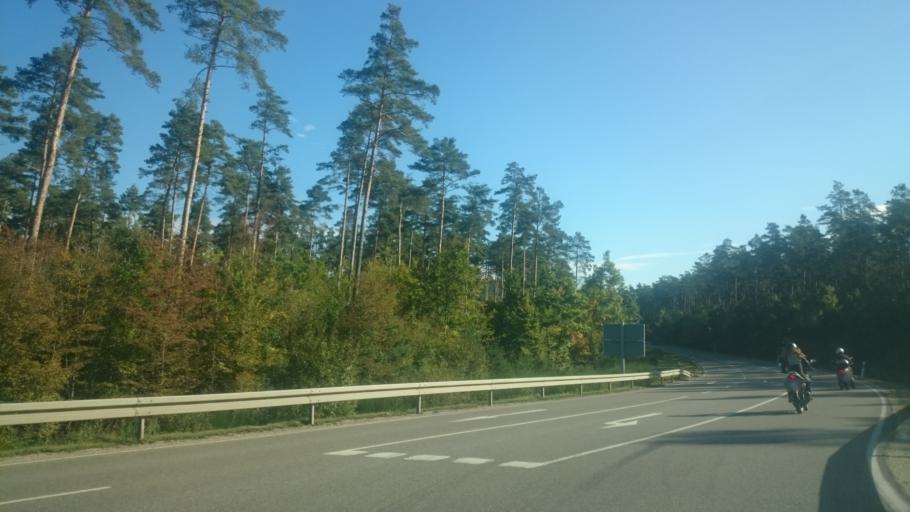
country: DE
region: Bavaria
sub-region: Regierungsbezirk Mittelfranken
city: Rottenbach
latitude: 49.1312
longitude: 11.0284
